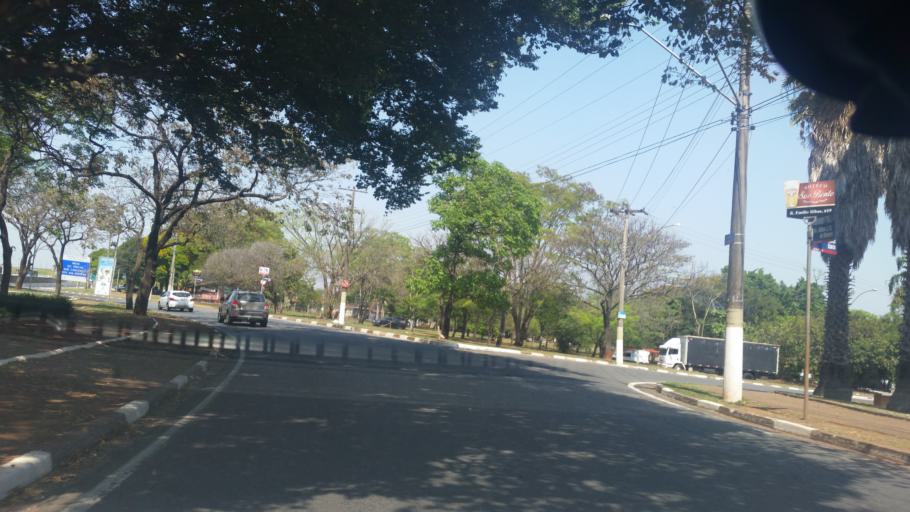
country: BR
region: Sao Paulo
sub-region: Campinas
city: Campinas
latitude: -22.8337
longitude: -47.0793
